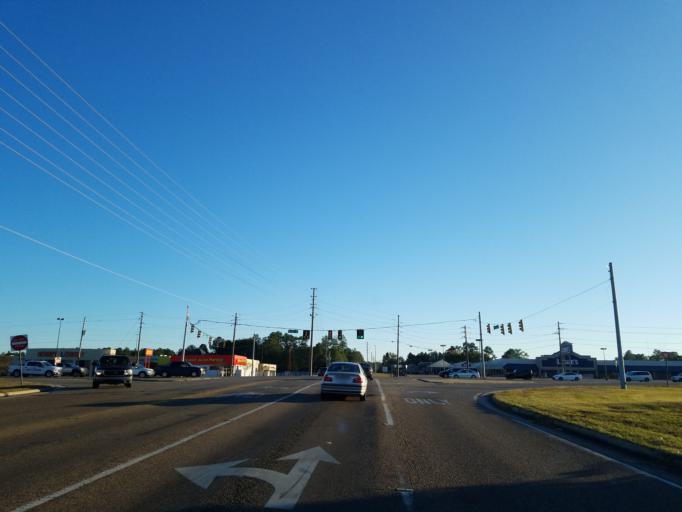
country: US
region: Mississippi
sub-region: Lamar County
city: West Hattiesburg
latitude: 31.3230
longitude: -89.3735
